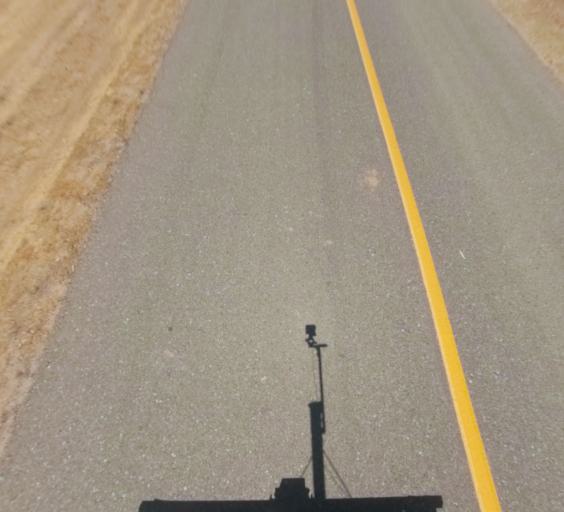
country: US
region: California
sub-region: Madera County
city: Madera Acres
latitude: 37.0611
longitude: -120.0181
